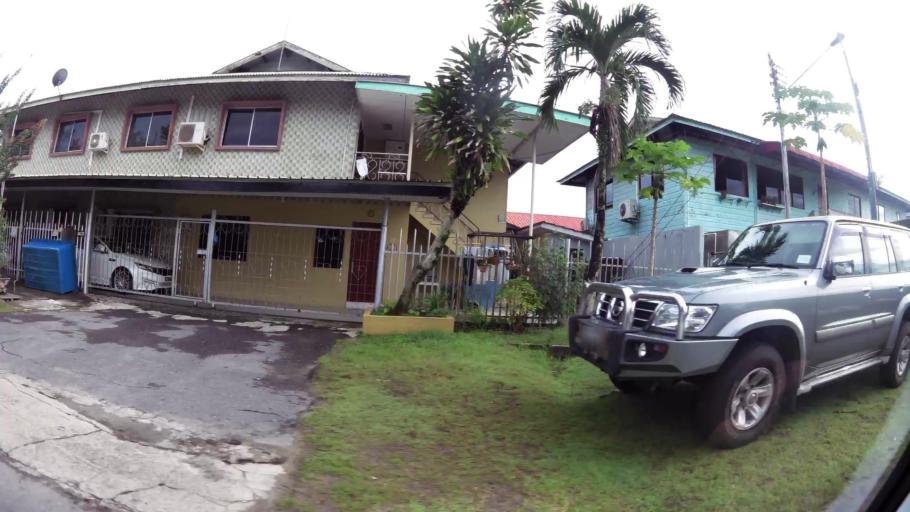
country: BN
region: Belait
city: Seria
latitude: 4.6144
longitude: 114.3490
